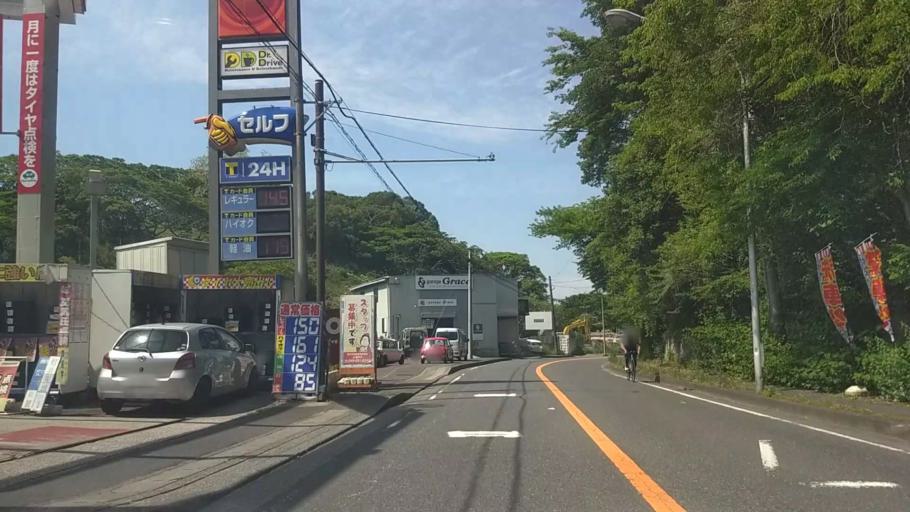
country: JP
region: Kanagawa
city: Kamakura
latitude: 35.3431
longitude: 139.5821
